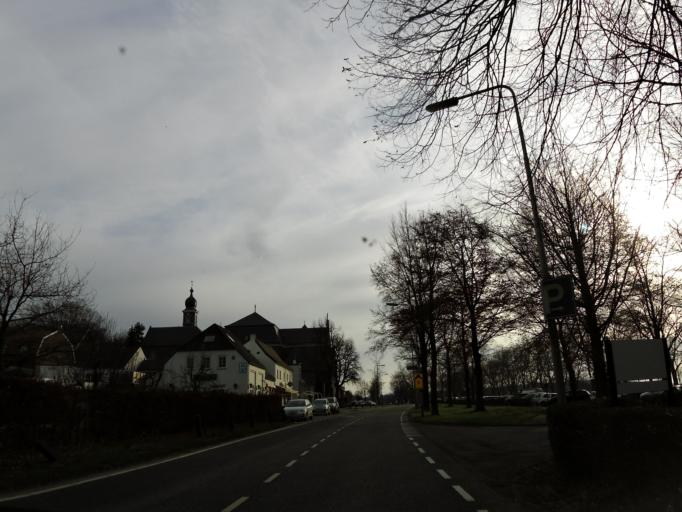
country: NL
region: Limburg
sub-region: Gemeente Voerendaal
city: Ubachsberg
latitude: 50.8144
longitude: 5.9108
